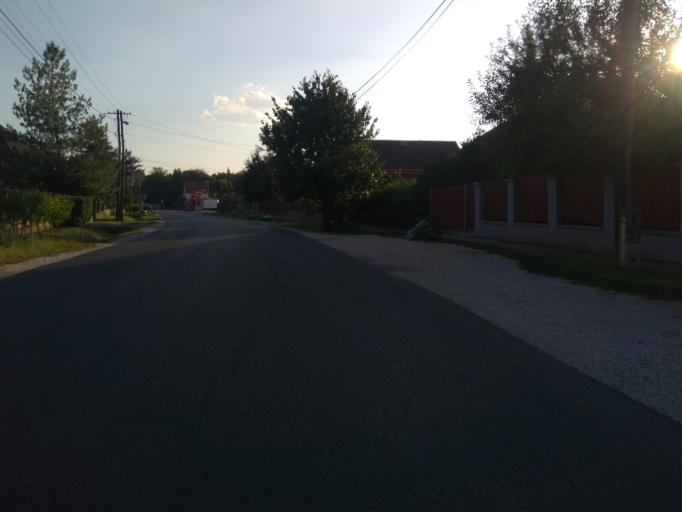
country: HU
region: Borsod-Abauj-Zemplen
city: Nyekladhaza
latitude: 47.9898
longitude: 20.8356
